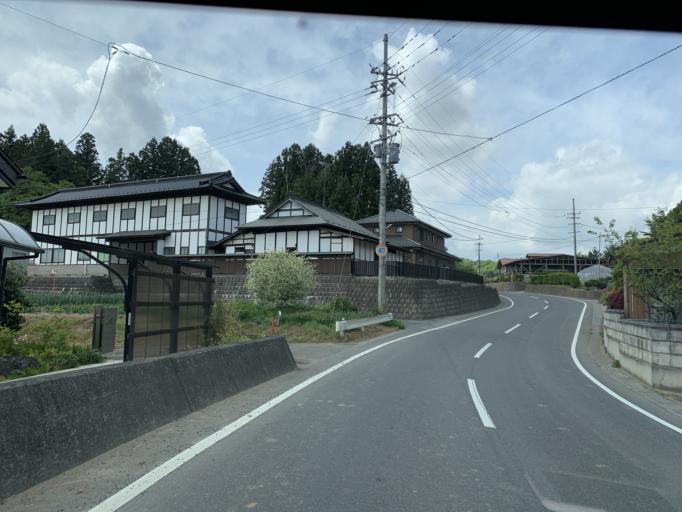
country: JP
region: Iwate
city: Ichinoseki
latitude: 38.7904
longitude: 141.0027
